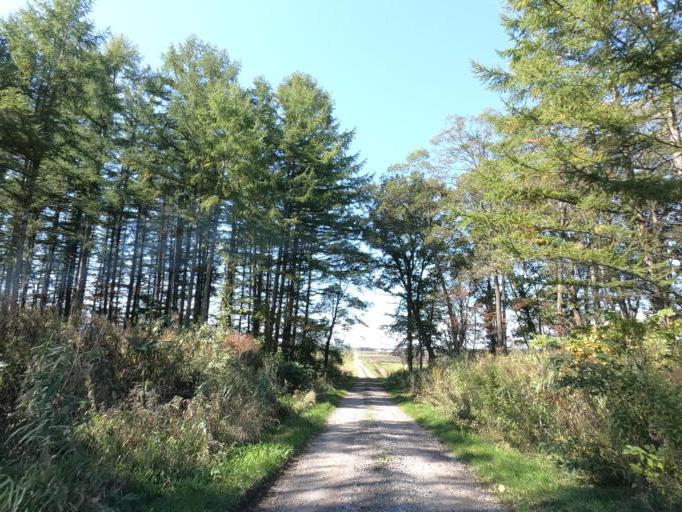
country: JP
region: Hokkaido
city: Otofuke
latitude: 43.0712
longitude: 143.2633
